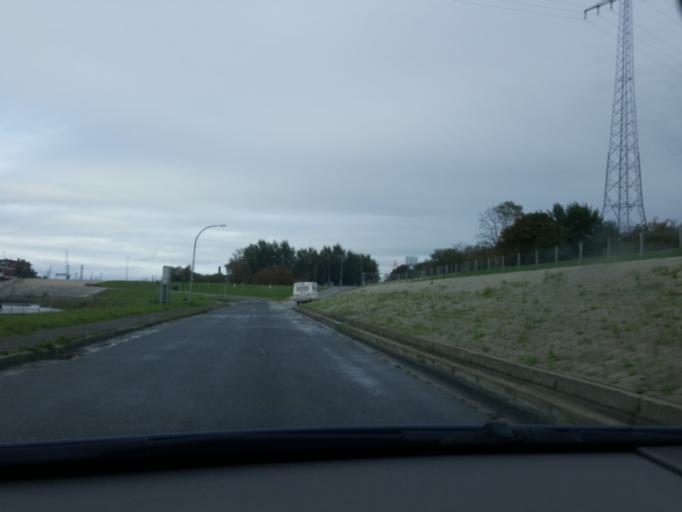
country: DE
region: Lower Saxony
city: Emden
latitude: 53.3426
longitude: 7.1898
